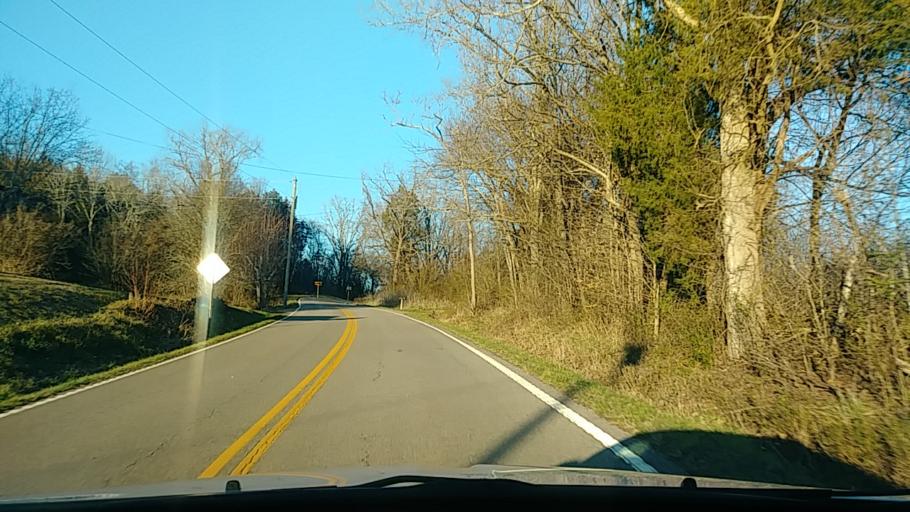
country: US
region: Tennessee
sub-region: Greene County
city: Mosheim
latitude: 36.1262
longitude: -83.1134
